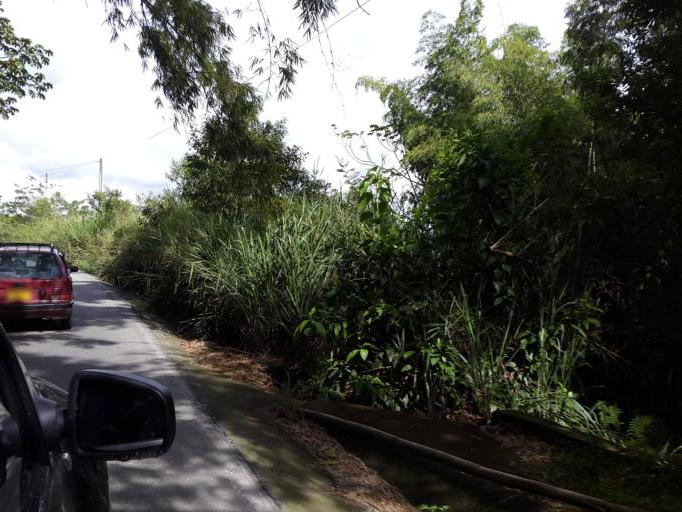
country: CO
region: Quindio
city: Cordoba
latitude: 4.4065
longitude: -75.7268
